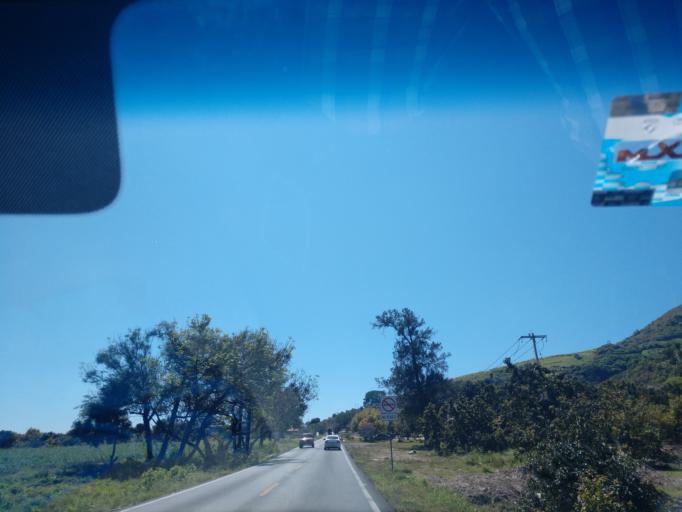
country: MX
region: Nayarit
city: Xalisco
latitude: 21.4129
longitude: -104.8973
